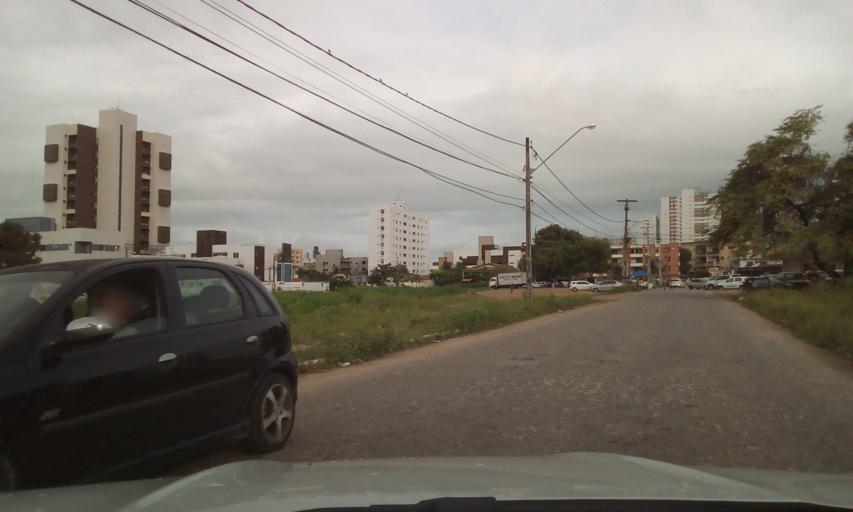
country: BR
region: Paraiba
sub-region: Joao Pessoa
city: Joao Pessoa
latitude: -7.0754
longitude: -34.8393
